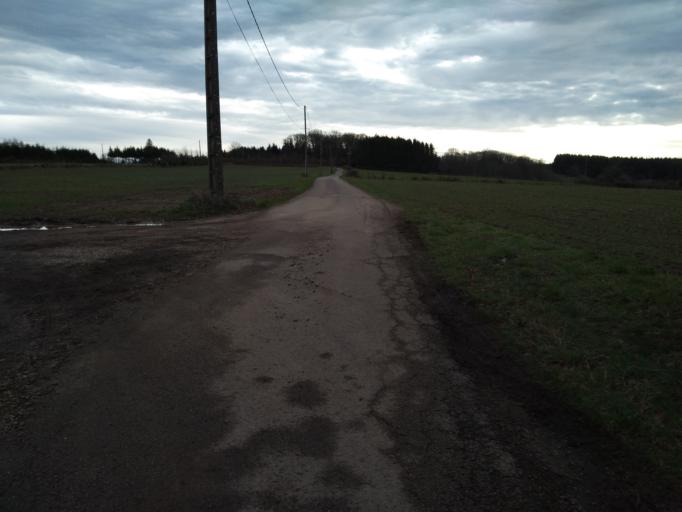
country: FR
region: Bourgogne
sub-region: Departement de la Cote-d'Or
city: Saulieu
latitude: 47.2787
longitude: 4.1541
